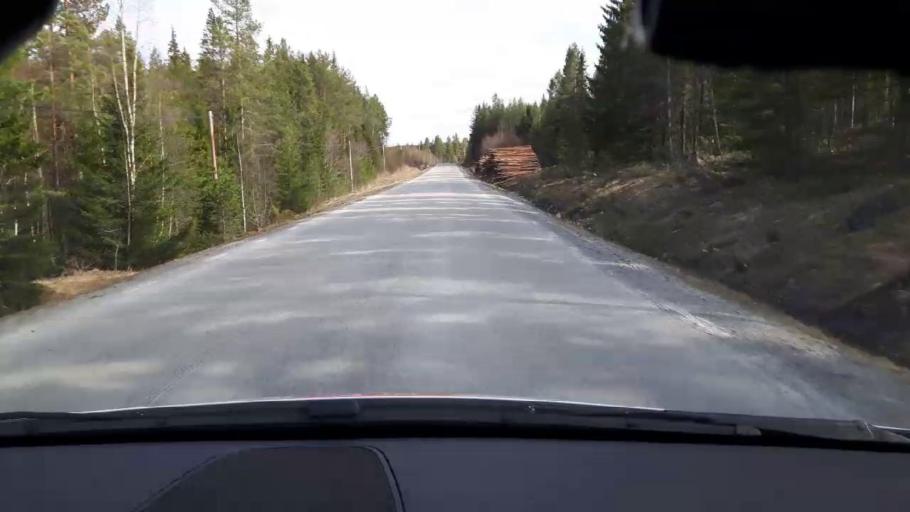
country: SE
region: Jaemtland
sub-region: Bergs Kommun
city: Hoverberg
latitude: 62.7371
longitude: 14.5899
